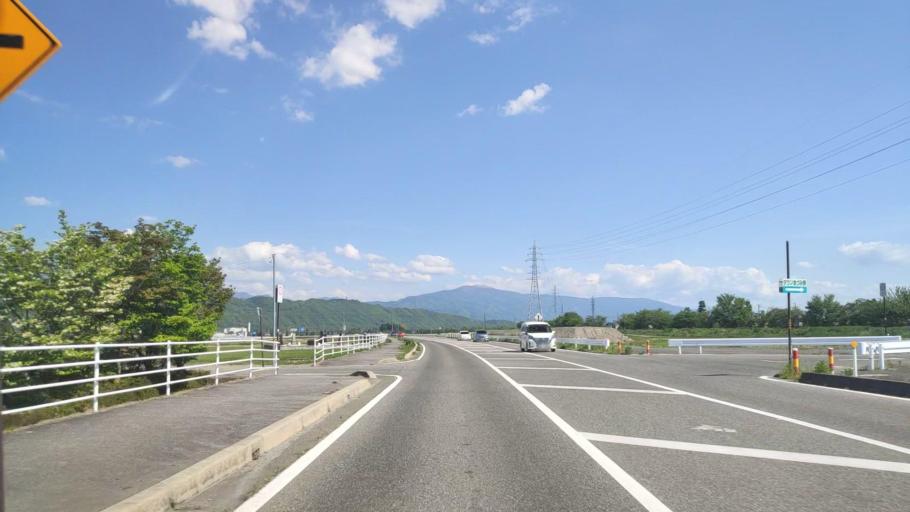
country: JP
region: Nagano
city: Toyoshina
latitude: 36.2832
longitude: 137.9122
